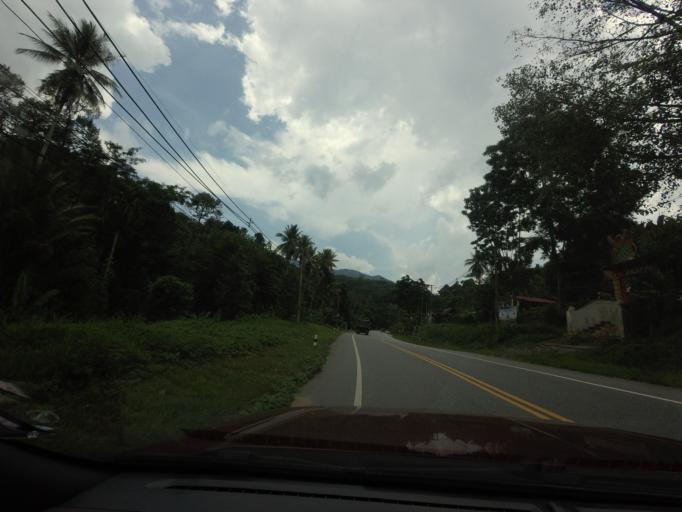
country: TH
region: Yala
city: Than To
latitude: 6.0777
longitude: 101.1884
